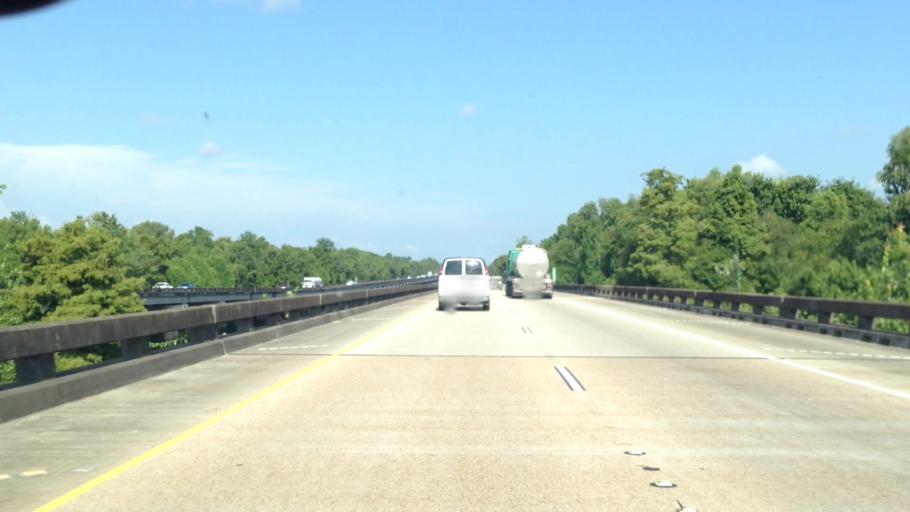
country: US
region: Louisiana
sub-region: Saint John the Baptist Parish
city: Reserve
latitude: 30.1115
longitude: -90.5470
